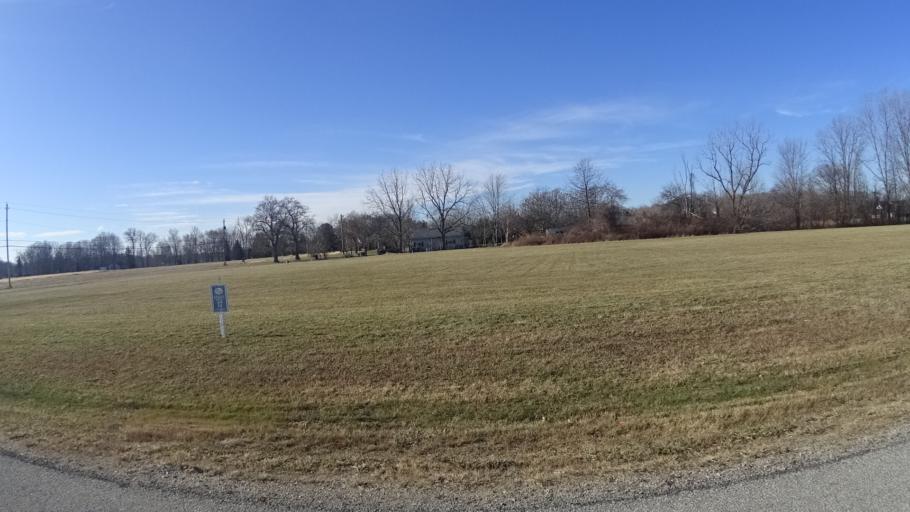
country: US
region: Ohio
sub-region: Lorain County
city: South Amherst
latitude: 41.3538
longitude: -82.3277
